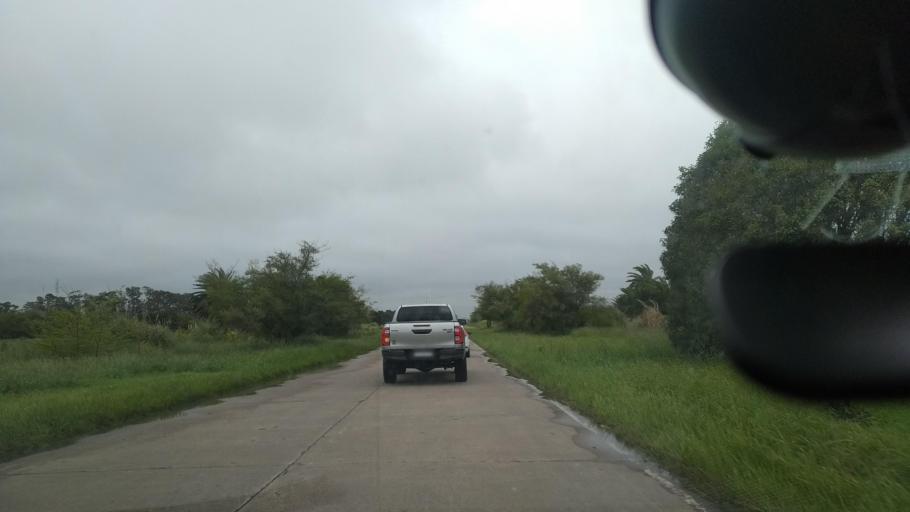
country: AR
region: Buenos Aires
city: Veronica
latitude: -35.5373
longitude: -57.3187
